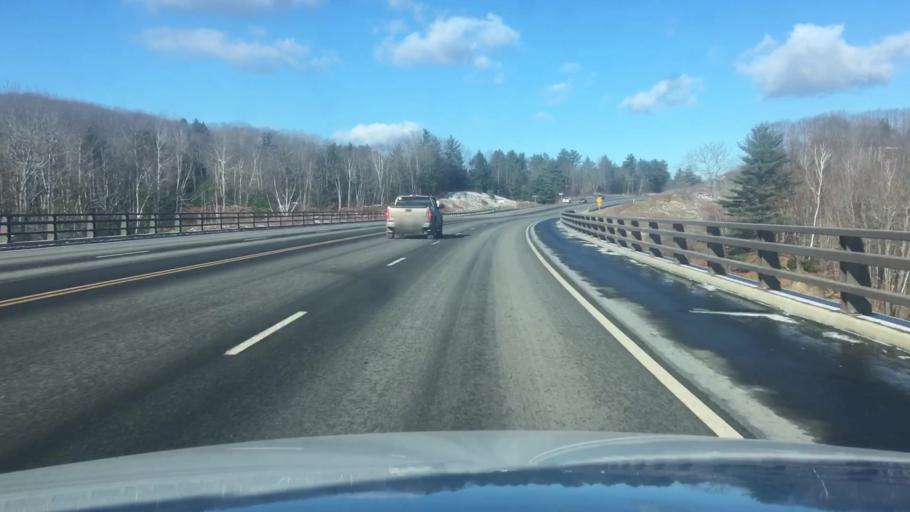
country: US
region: Maine
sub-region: Kennebec County
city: Augusta
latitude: 44.3358
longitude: -69.7651
